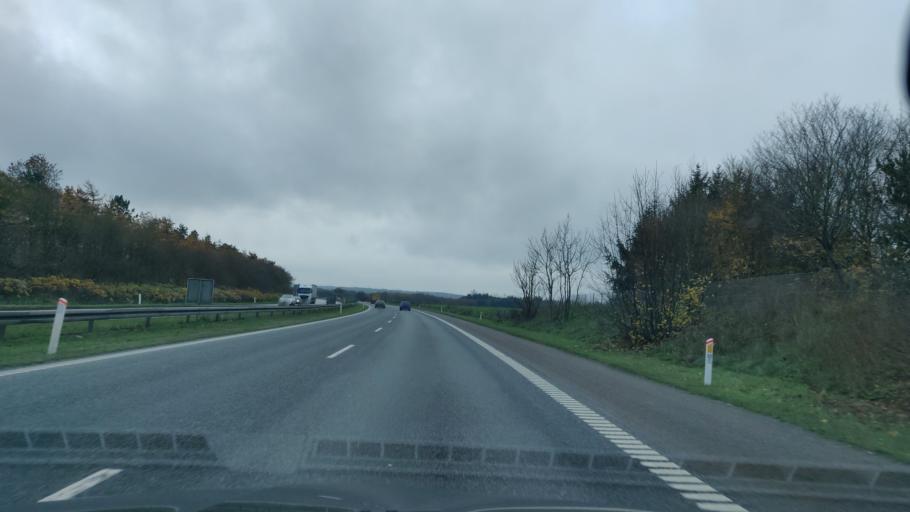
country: DK
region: North Denmark
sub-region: Alborg Kommune
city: Svenstrup
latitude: 56.9860
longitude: 9.8847
